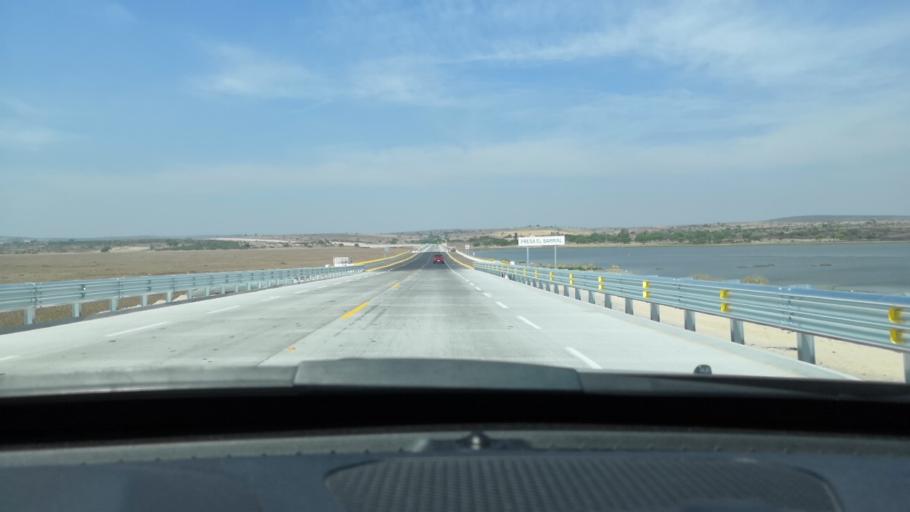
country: MX
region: Guanajuato
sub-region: Purisima del Rincon
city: Potrerillos (Guanajal)
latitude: 21.0838
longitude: -101.8405
